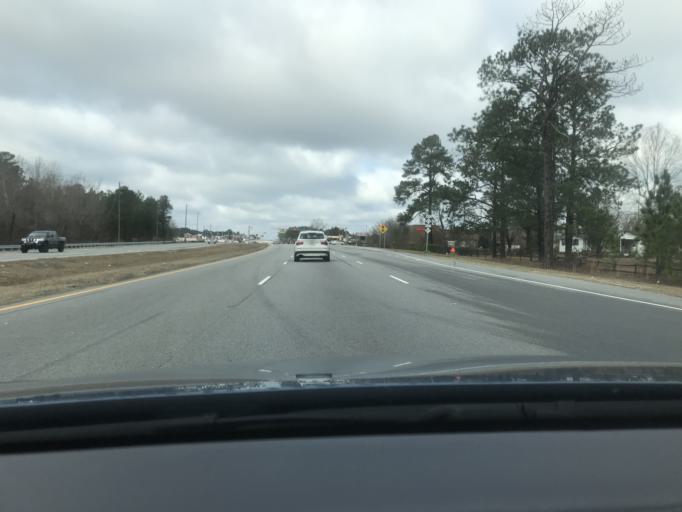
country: US
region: North Carolina
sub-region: Cumberland County
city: Spring Lake
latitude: 35.2524
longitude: -79.0281
